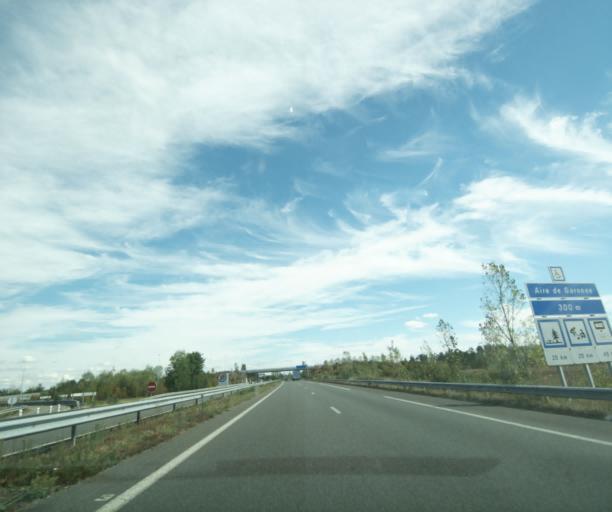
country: FR
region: Midi-Pyrenees
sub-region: Departement du Tarn-et-Garonne
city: Saint-Nicolas-de-la-Grave
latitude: 44.0446
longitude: 0.9958
